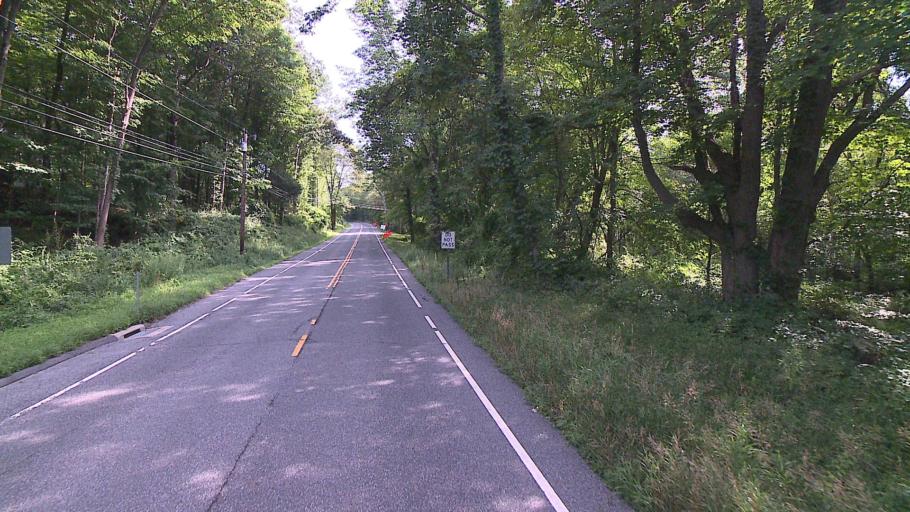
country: US
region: Connecticut
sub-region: Fairfield County
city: Sherman
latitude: 41.5317
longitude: -73.5072
